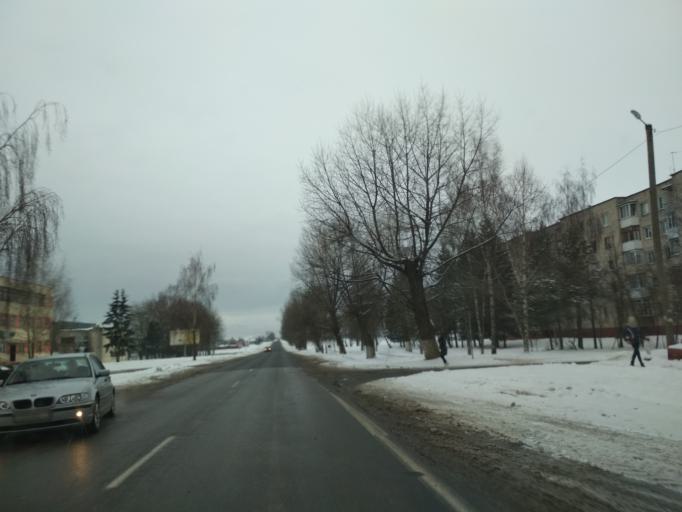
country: BY
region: Minsk
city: Mar''ina Horka
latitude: 53.5149
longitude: 28.1290
